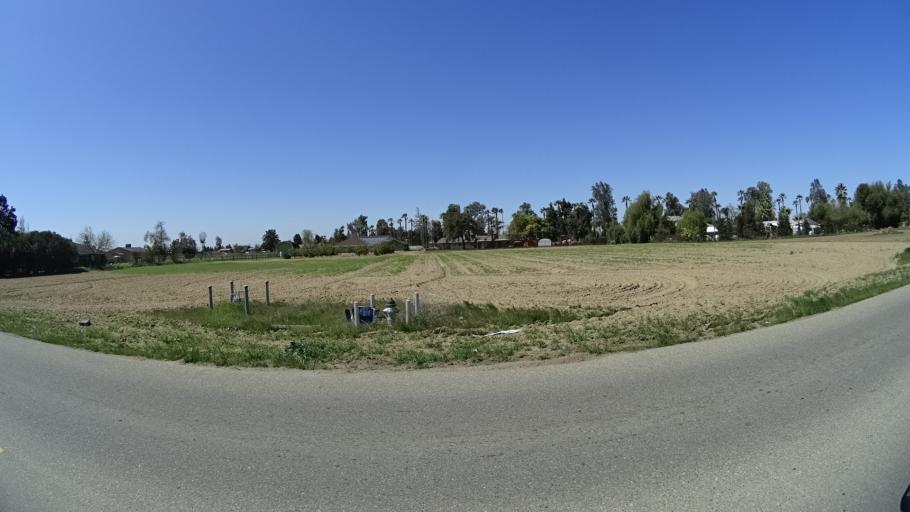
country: US
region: California
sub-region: Fresno County
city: West Park
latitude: 36.7251
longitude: -119.8444
